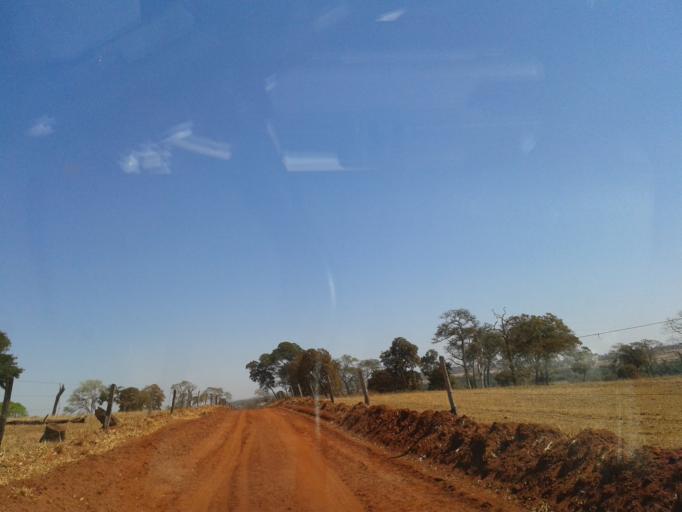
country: BR
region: Minas Gerais
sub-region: Santa Vitoria
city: Santa Vitoria
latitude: -19.0745
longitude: -50.0603
